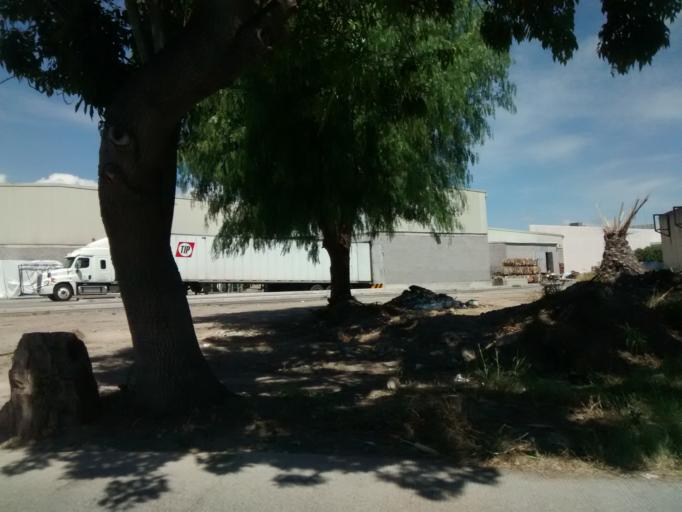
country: MX
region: Puebla
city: Tehuacan
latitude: 18.4685
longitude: -97.4147
